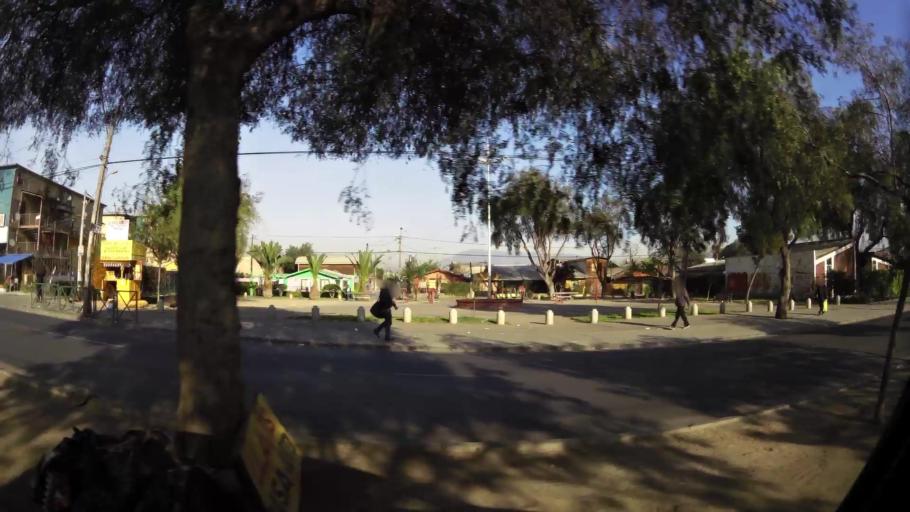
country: CL
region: Santiago Metropolitan
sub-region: Provincia de Santiago
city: Lo Prado
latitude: -33.4425
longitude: -70.7405
